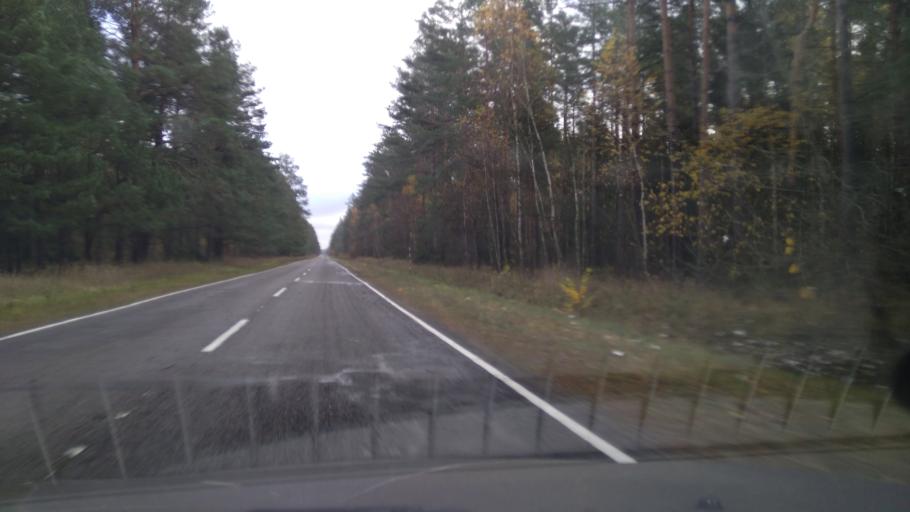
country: BY
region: Minsk
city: Slutsk
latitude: 53.2303
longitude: 27.6855
